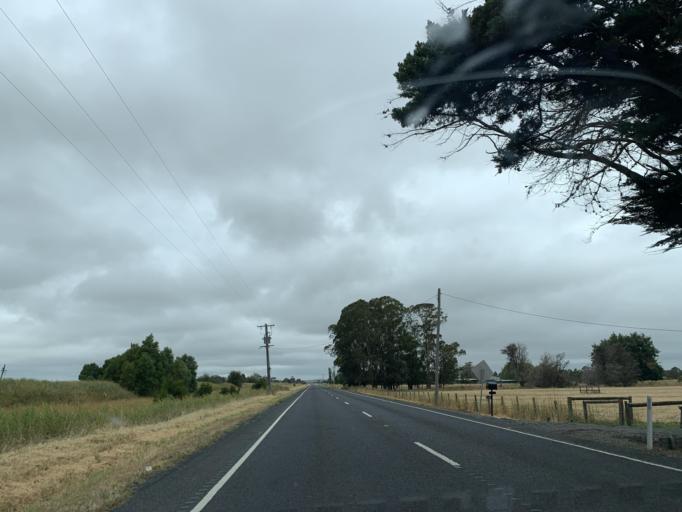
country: AU
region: Victoria
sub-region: Cardinia
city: Garfield
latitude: -38.1867
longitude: 145.6306
